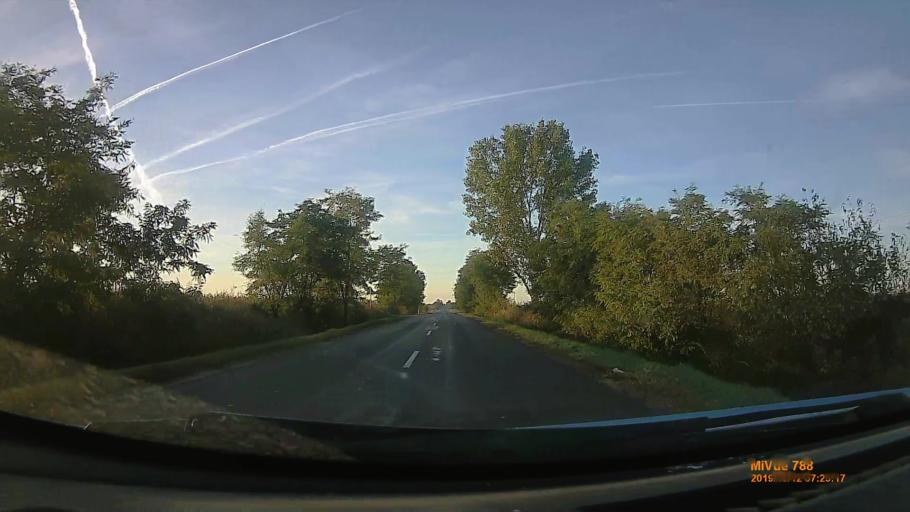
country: HU
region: Hajdu-Bihar
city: Monostorpalyi
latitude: 47.3507
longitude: 21.7664
